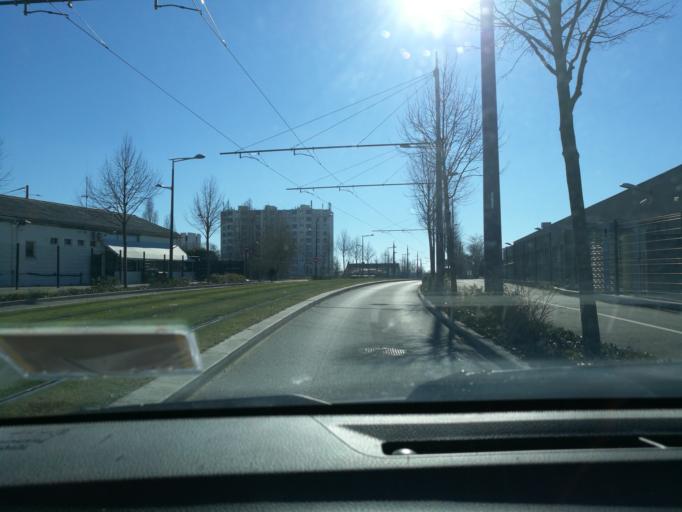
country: FR
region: Centre
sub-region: Departement du Loiret
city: Saint-Jean-de-la-Ruelle
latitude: 47.9011
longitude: 1.8748
